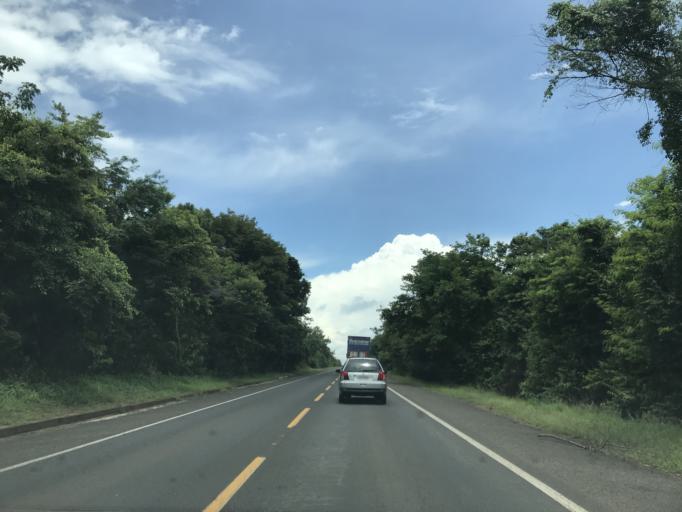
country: BR
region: Minas Gerais
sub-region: Frutal
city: Frutal
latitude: -19.6896
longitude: -48.9847
